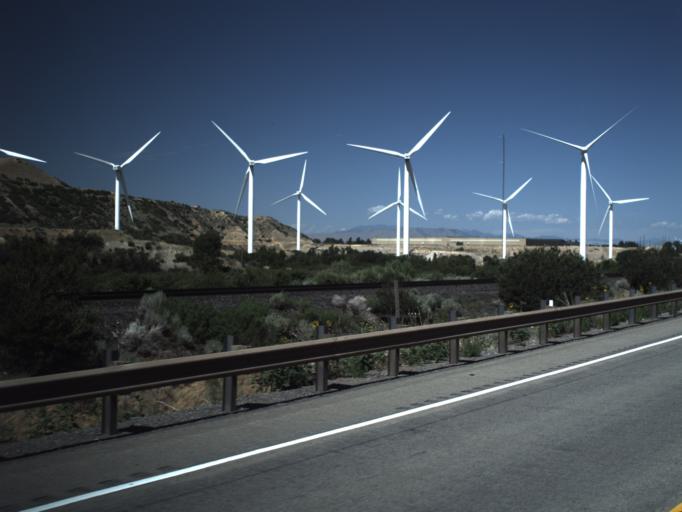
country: US
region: Utah
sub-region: Utah County
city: Mapleton
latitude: 40.0689
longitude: -111.5750
